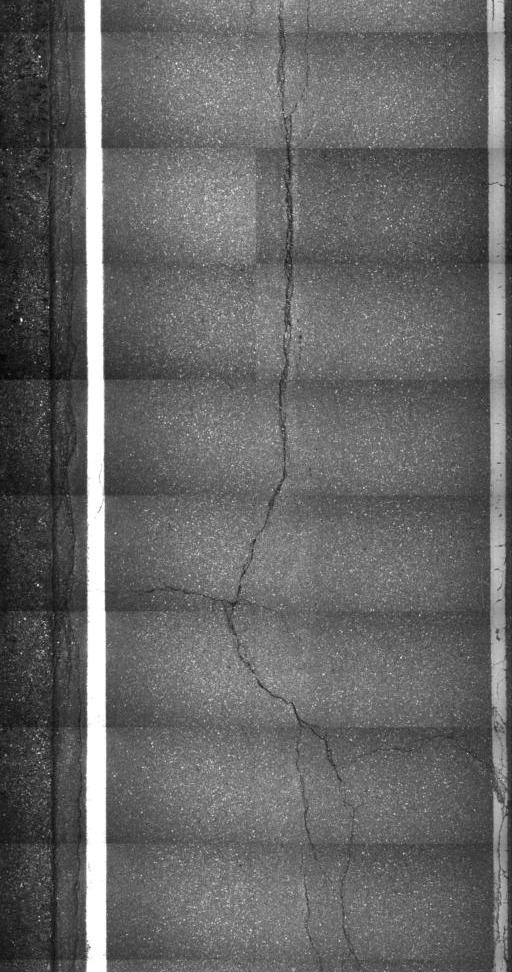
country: US
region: Vermont
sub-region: Windsor County
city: Woodstock
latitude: 43.5429
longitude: -72.7175
